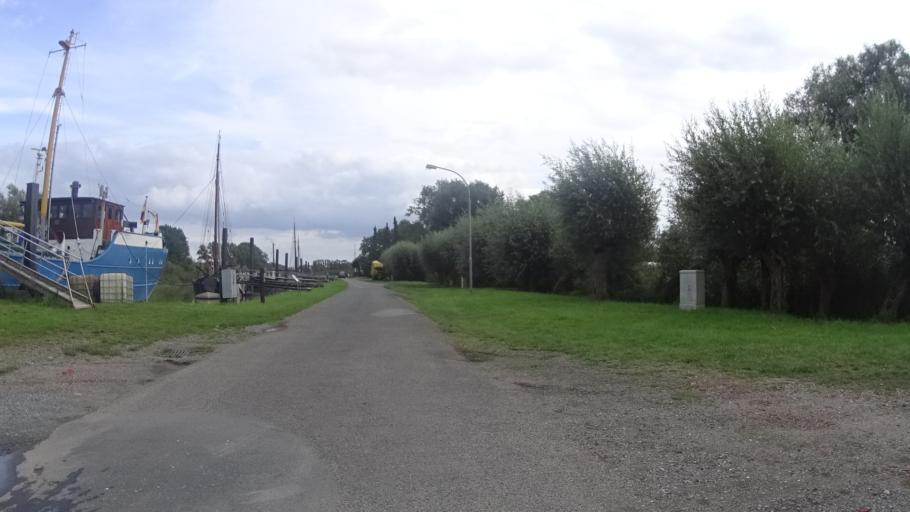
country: DE
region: Lower Saxony
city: Wischhafen
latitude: 53.7735
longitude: 9.3220
